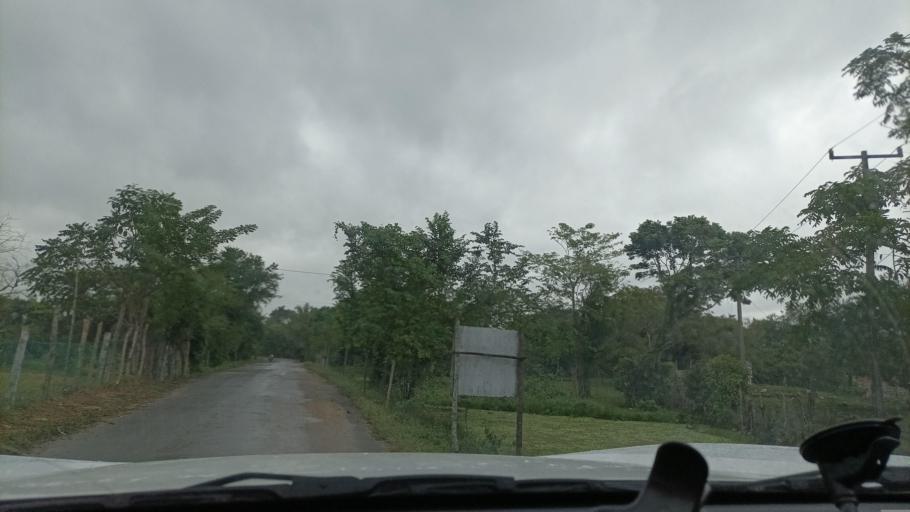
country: MX
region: Veracruz
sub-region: Moloacan
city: Cuichapa
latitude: 17.7546
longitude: -94.3937
